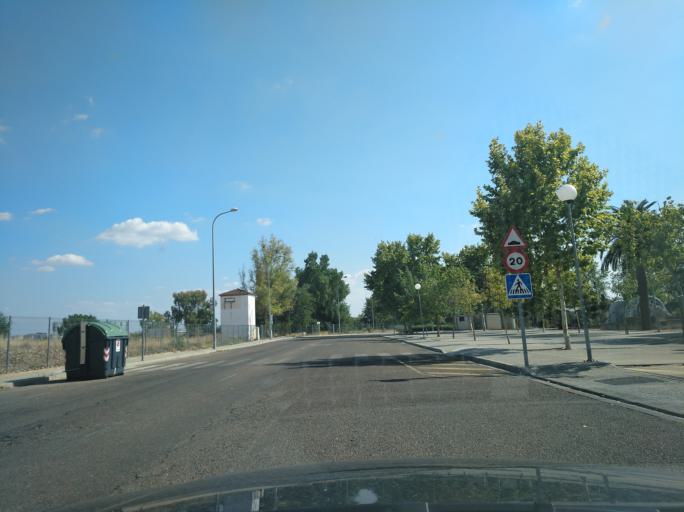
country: ES
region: Extremadura
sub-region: Provincia de Badajoz
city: Badajoz
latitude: 38.8841
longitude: -7.0031
